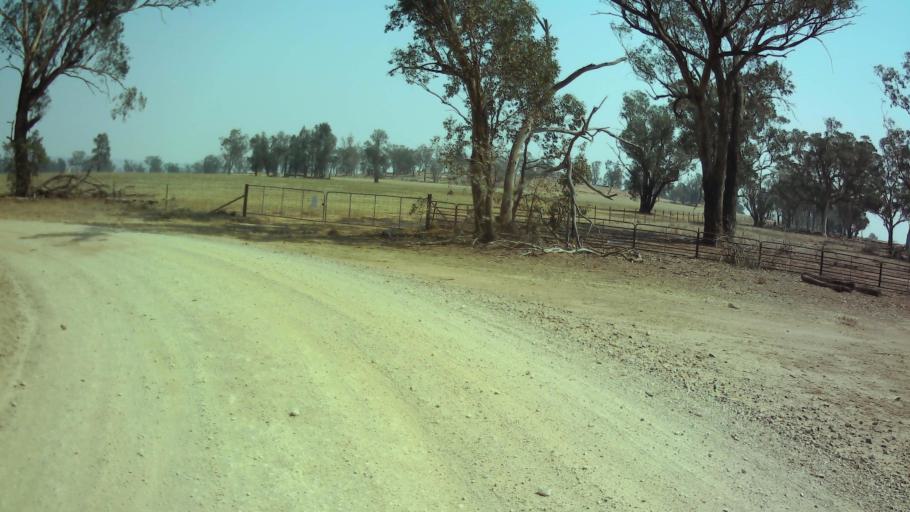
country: AU
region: New South Wales
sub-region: Weddin
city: Grenfell
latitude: -33.6466
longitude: 148.2701
